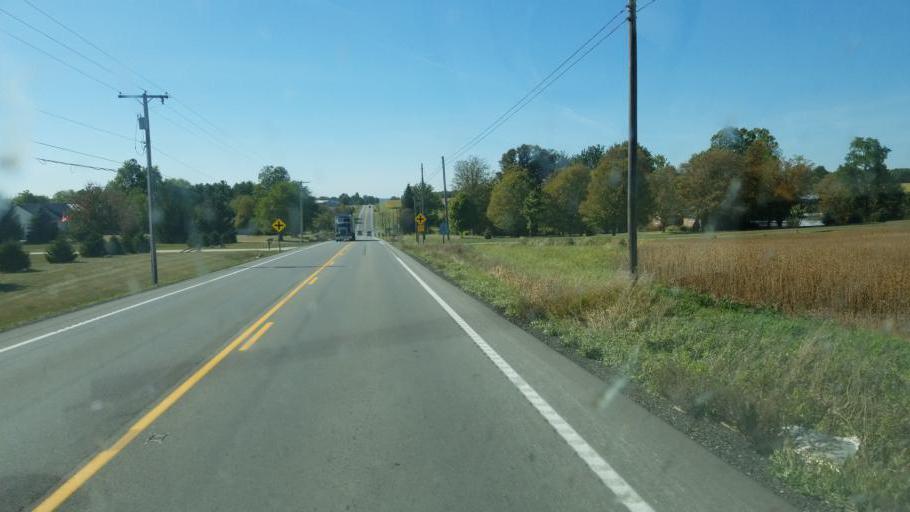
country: US
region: Ohio
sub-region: Ashland County
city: Ashland
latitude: 40.8567
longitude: -82.2080
